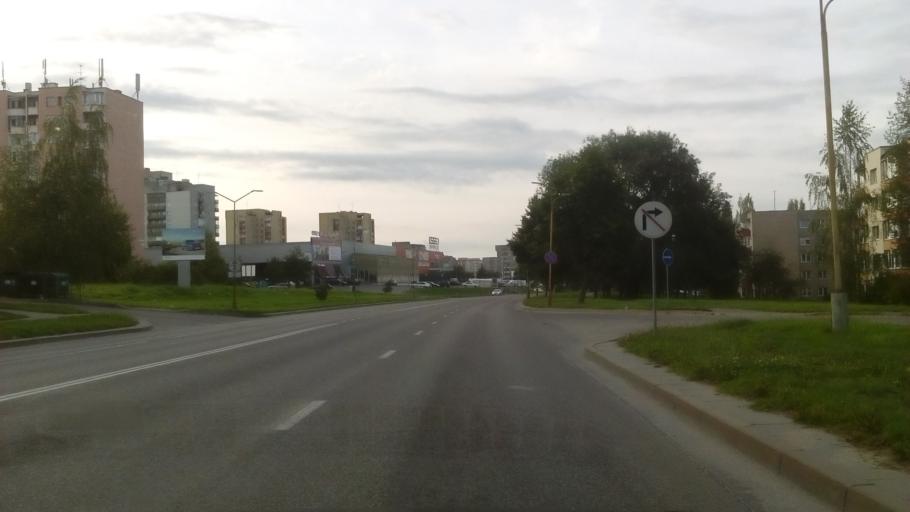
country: LT
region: Alytaus apskritis
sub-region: Alytus
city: Alytus
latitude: 54.3915
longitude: 24.0208
